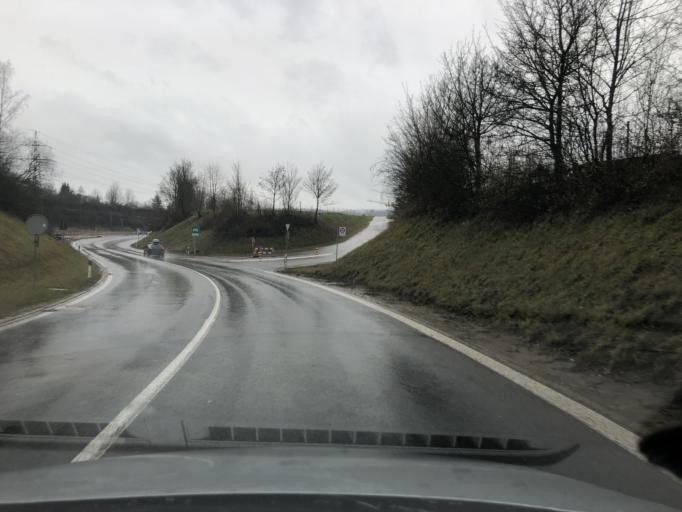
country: CH
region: Aargau
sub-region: Bezirk Brugg
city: Hausen
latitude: 47.4690
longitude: 8.2085
